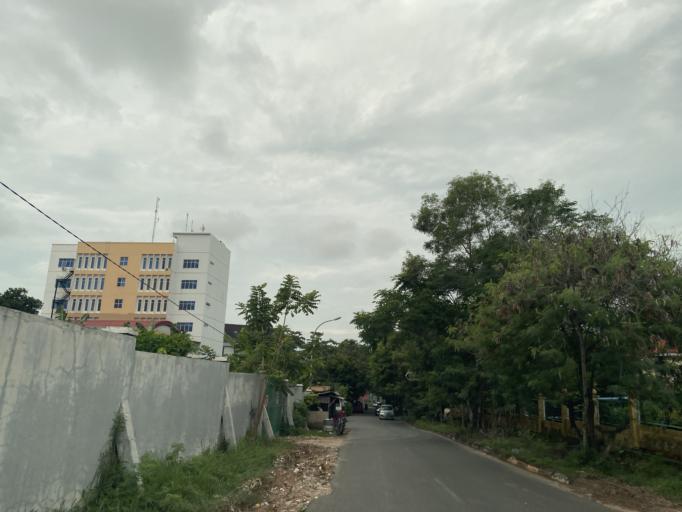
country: SG
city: Singapore
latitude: 1.1239
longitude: 104.0562
